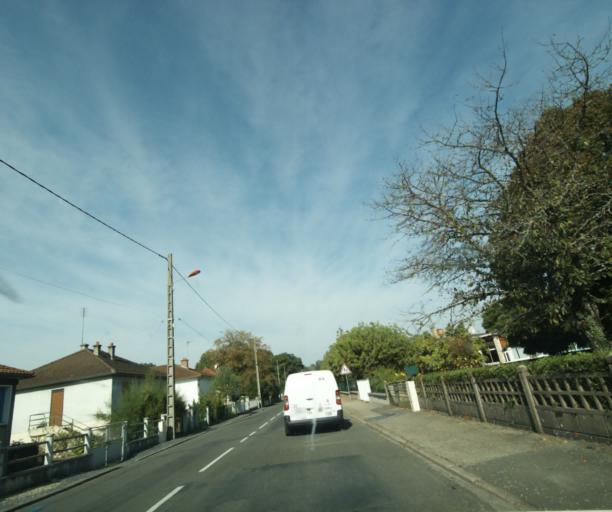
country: FR
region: Bourgogne
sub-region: Departement de Saone-et-Loire
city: Genelard
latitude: 46.5790
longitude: 4.2422
